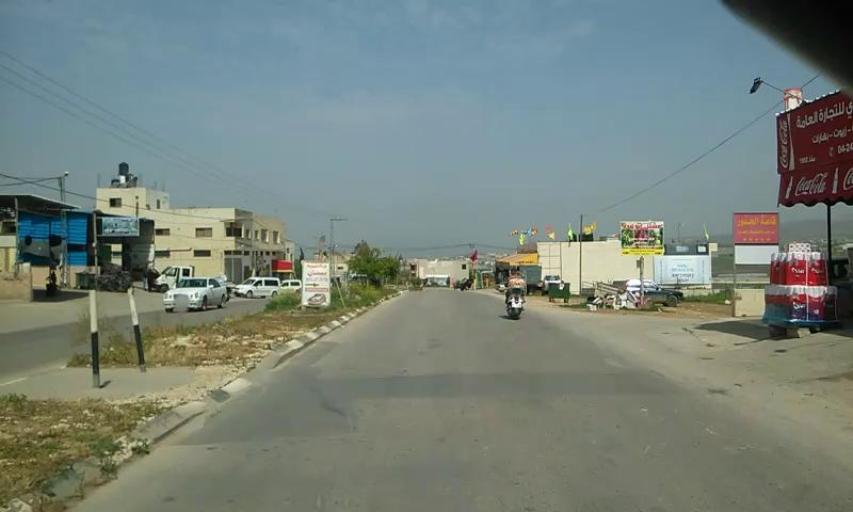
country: PS
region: West Bank
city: Al Jalamah
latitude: 32.4898
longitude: 35.3009
